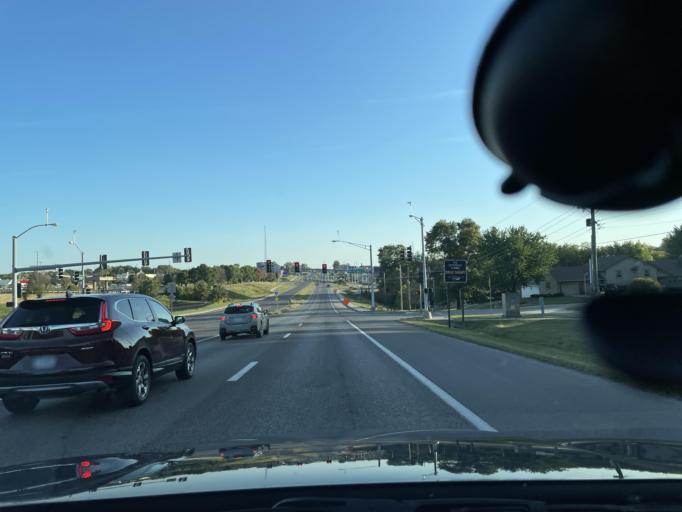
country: US
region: Missouri
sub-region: Andrew County
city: Country Club Village
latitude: 39.8116
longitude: -94.8153
